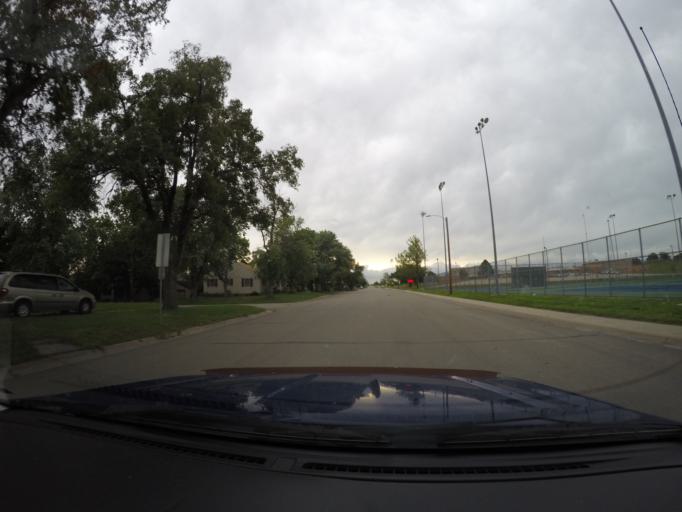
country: US
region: Kansas
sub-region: Clay County
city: Clay Center
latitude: 39.3842
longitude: -97.1190
